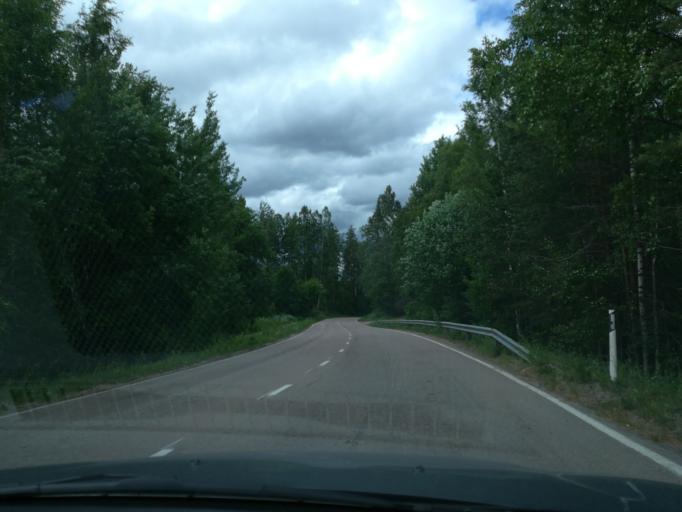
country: FI
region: South Karelia
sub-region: Lappeenranta
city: Savitaipale
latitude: 61.1980
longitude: 27.6959
